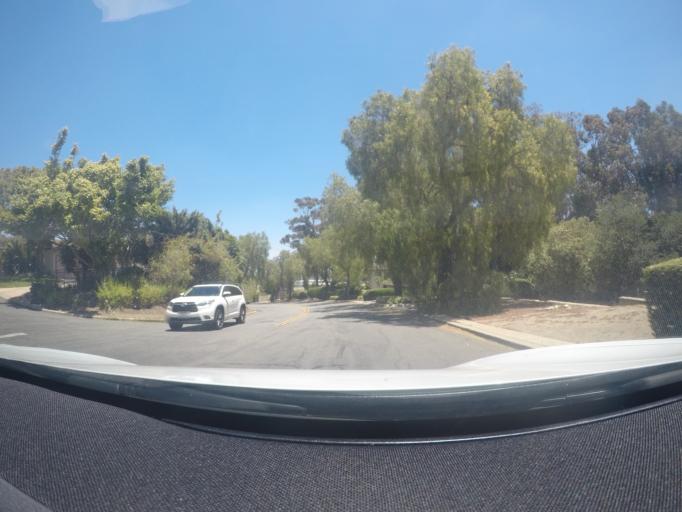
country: US
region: California
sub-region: Los Angeles County
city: Rolling Hills Estates
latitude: 33.7980
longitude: -118.3561
